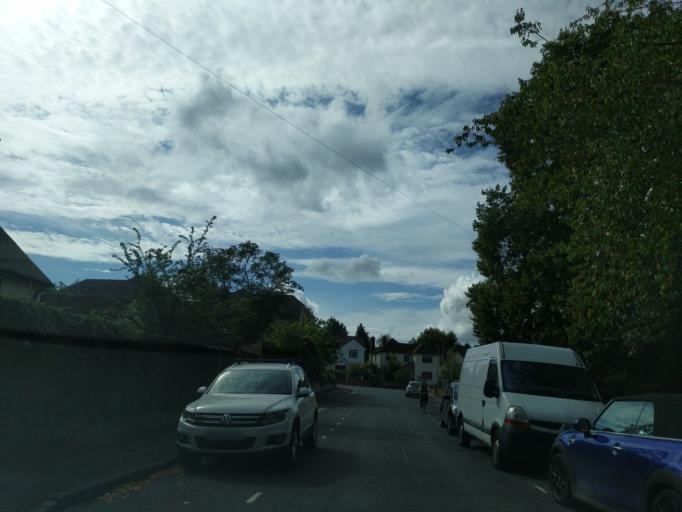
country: GB
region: England
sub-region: Oxfordshire
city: Oxford
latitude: 51.7636
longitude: -1.2229
